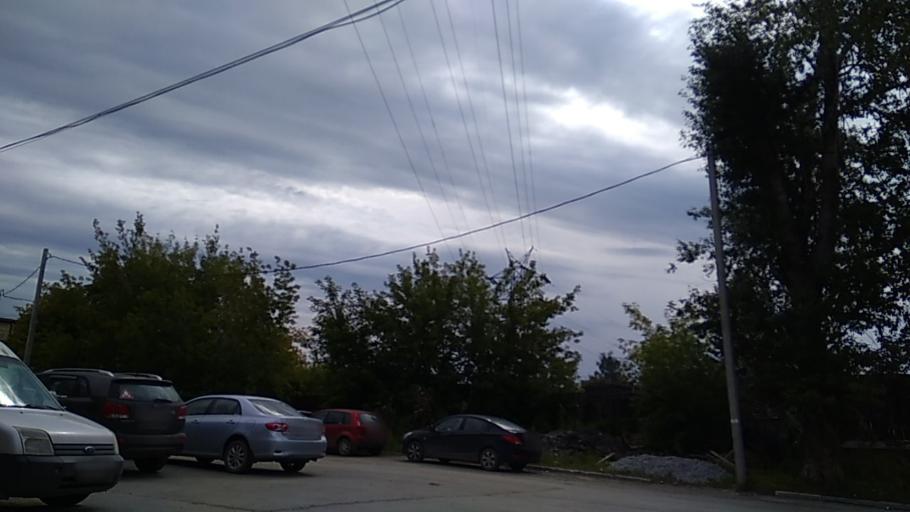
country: RU
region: Sverdlovsk
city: Yekaterinburg
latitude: 56.8827
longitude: 60.6226
